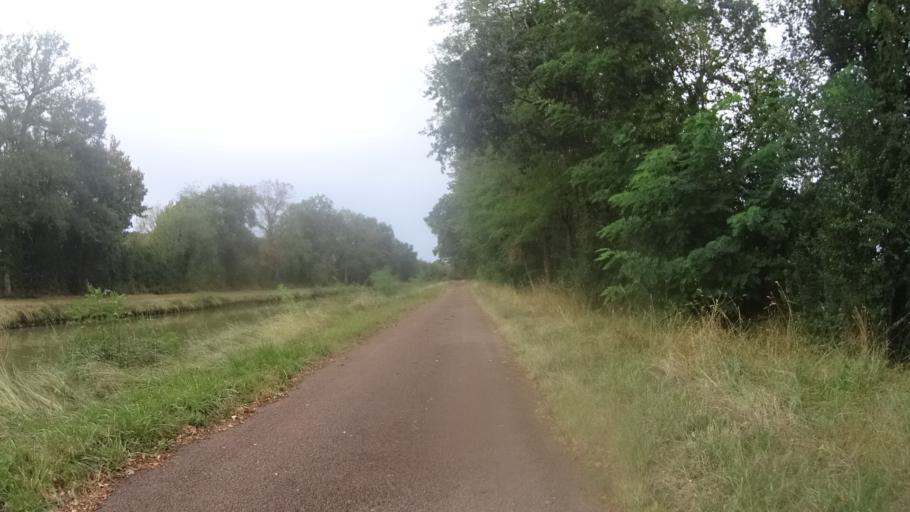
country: FR
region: Bourgogne
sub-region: Departement de la Nievre
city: Imphy
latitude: 46.8978
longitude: 3.2457
